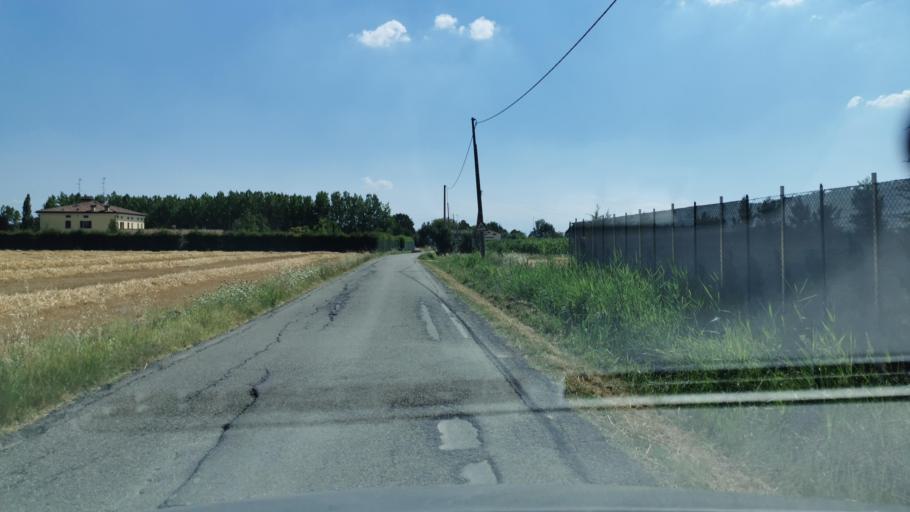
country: IT
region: Emilia-Romagna
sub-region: Provincia di Modena
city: Fossoli
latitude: 44.8074
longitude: 10.8962
